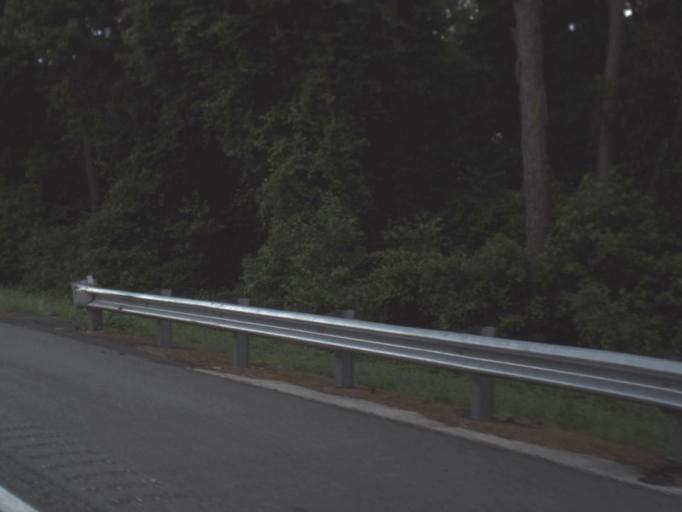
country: US
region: Florida
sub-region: Alachua County
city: High Springs
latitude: 29.9407
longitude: -82.5647
